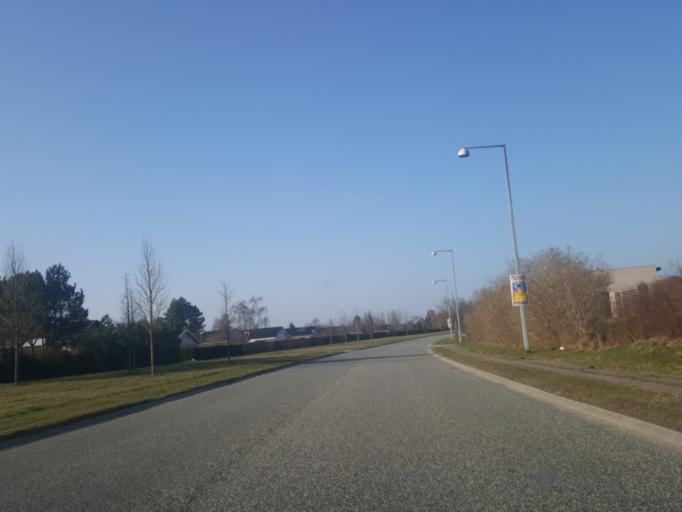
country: DK
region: Capital Region
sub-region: Allerod Kommune
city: Lillerod
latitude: 55.8685
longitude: 12.3283
